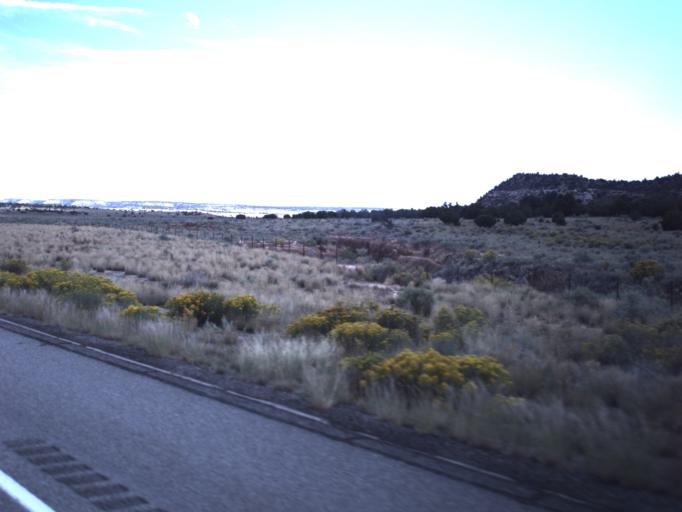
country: US
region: Utah
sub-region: Emery County
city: Castle Dale
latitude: 38.8737
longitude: -110.7384
